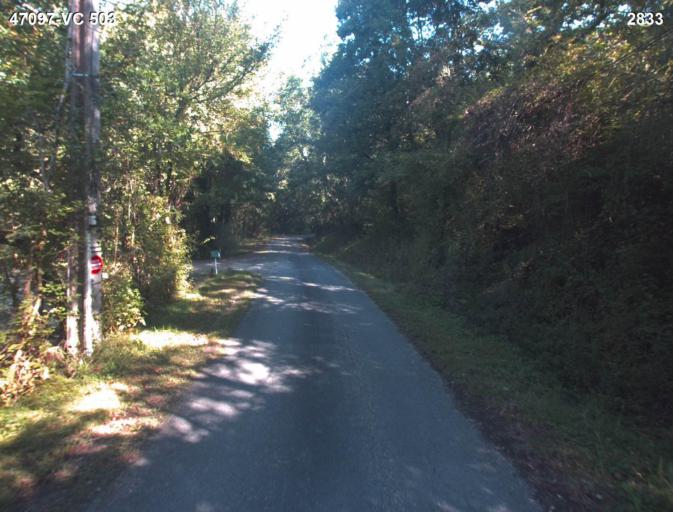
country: FR
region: Aquitaine
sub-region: Departement du Lot-et-Garonne
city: Port-Sainte-Marie
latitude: 44.2143
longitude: 0.3714
